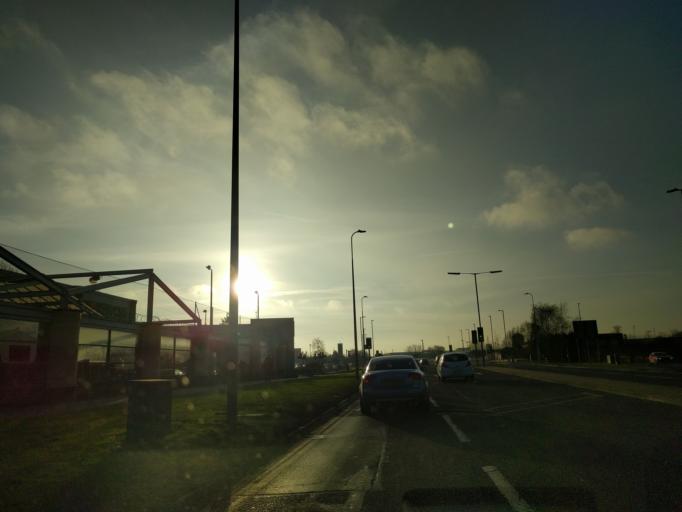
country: GB
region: England
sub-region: Lincolnshire
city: Lincoln
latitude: 53.2256
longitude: -0.5507
